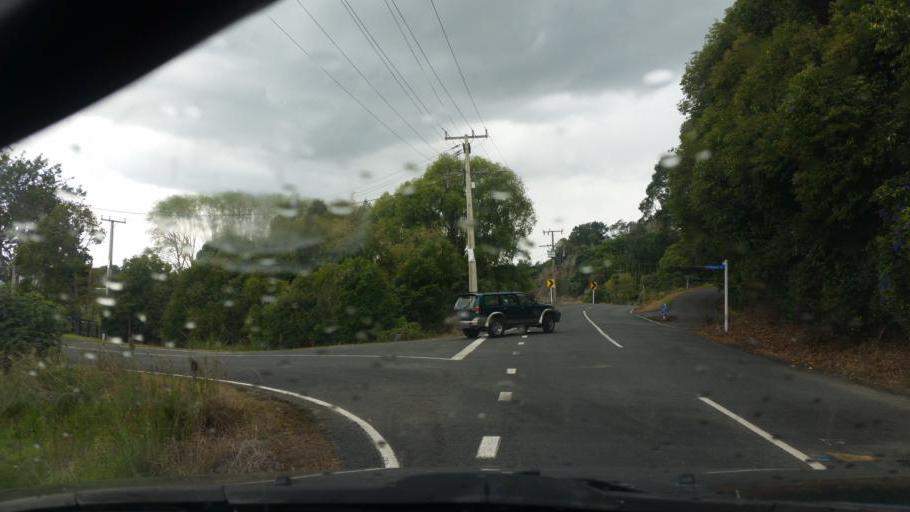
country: NZ
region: Northland
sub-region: Kaipara District
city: Dargaville
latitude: -35.9540
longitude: 173.8589
